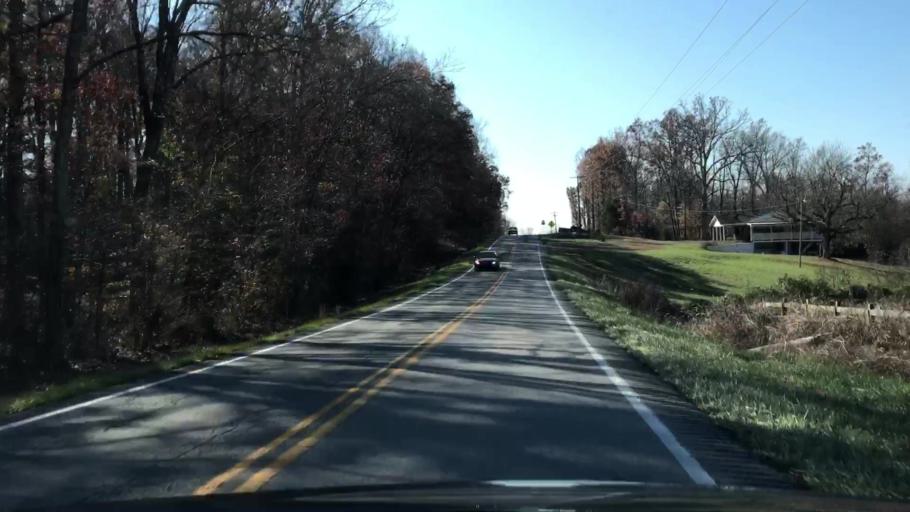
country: US
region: Kentucky
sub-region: Edmonson County
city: Brownsville
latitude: 37.3369
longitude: -86.2460
